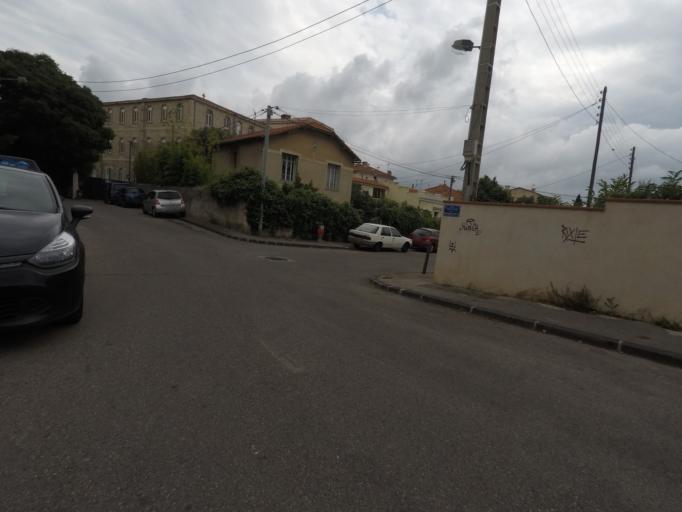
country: FR
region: Provence-Alpes-Cote d'Azur
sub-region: Departement des Bouches-du-Rhone
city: Marseille 08
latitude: 43.2629
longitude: 5.3911
